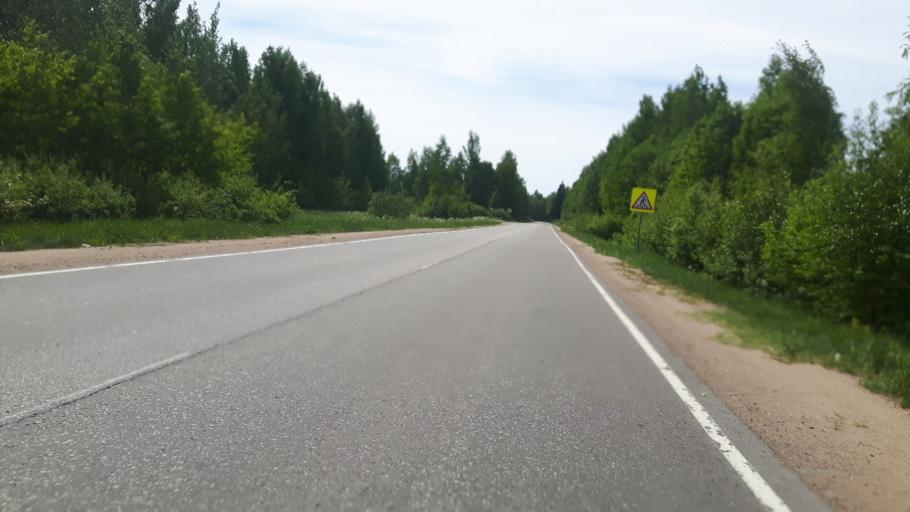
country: RU
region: Leningrad
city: Ust'-Luga
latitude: 59.6537
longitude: 28.2419
